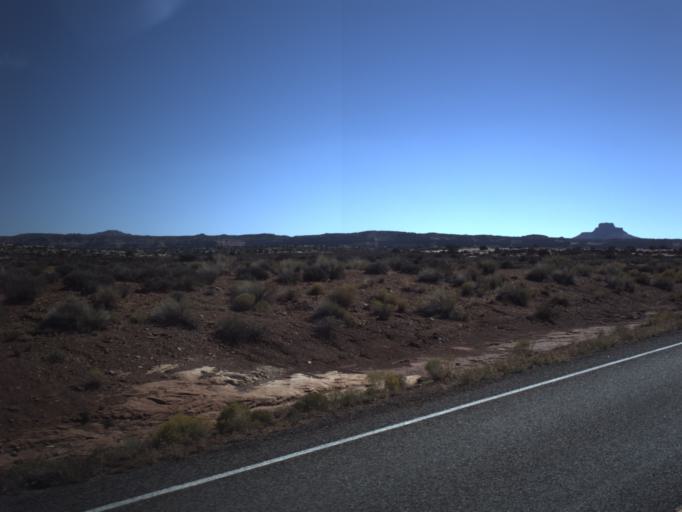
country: US
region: Utah
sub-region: San Juan County
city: Blanding
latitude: 37.7952
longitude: -110.3026
